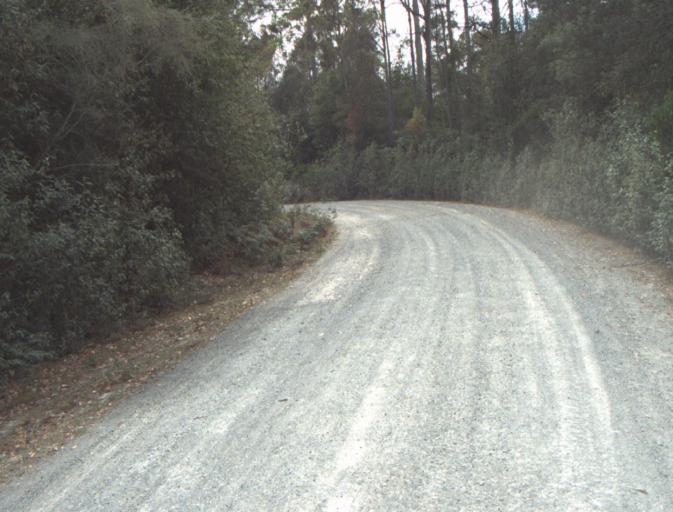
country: AU
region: Tasmania
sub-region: Launceston
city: Mayfield
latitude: -41.1943
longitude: 147.1595
